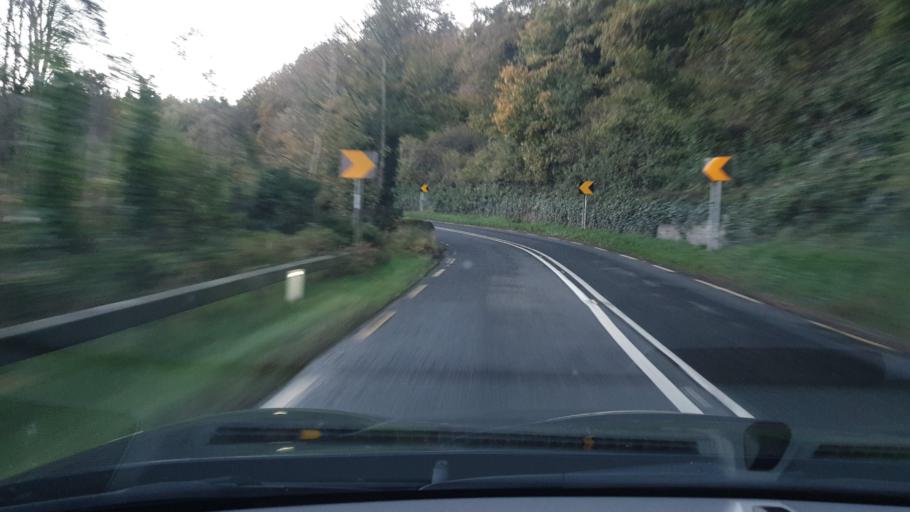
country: IE
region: Leinster
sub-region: Lu
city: Tullyallen
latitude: 53.7253
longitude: -6.4259
